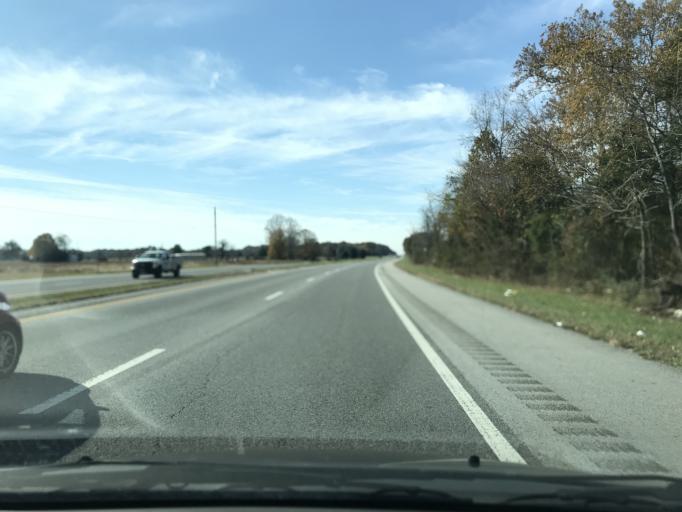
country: US
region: Tennessee
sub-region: Coffee County
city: Tullahoma
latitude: 35.3999
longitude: -86.1363
